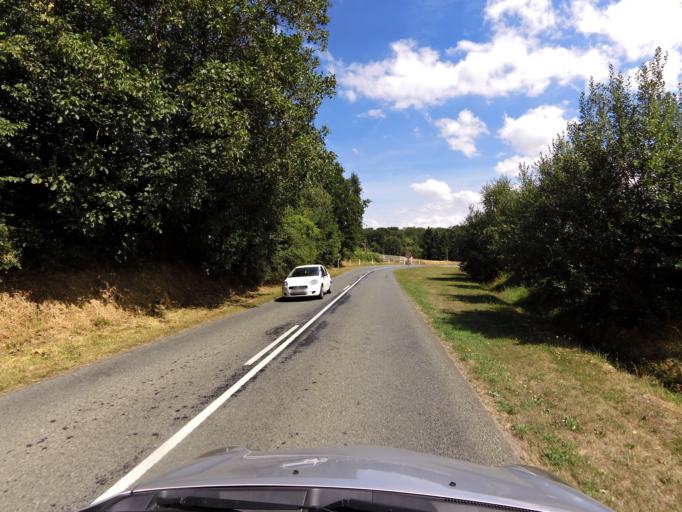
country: FR
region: Ile-de-France
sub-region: Departement de Seine-et-Marne
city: Crouy-sur-Ourcq
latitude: 49.1082
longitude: 3.0444
